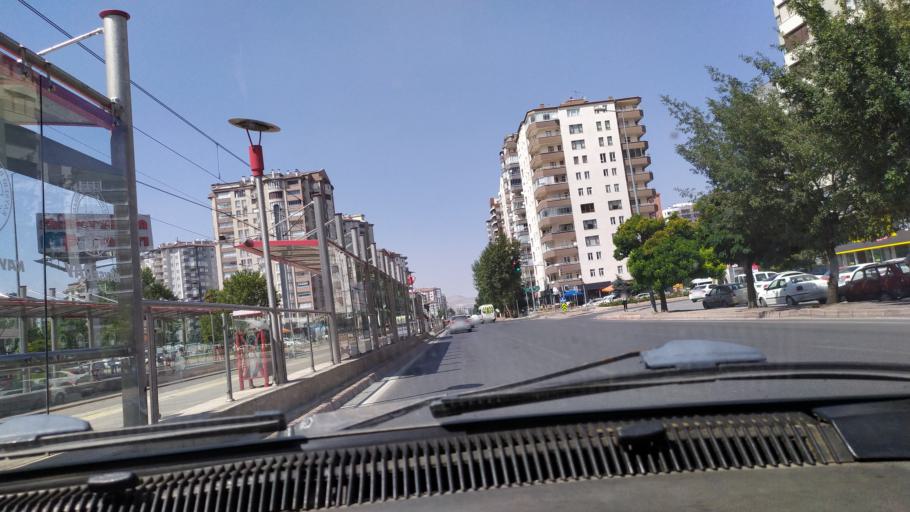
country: TR
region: Kayseri
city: Kayseri
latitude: 38.7271
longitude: 35.5261
